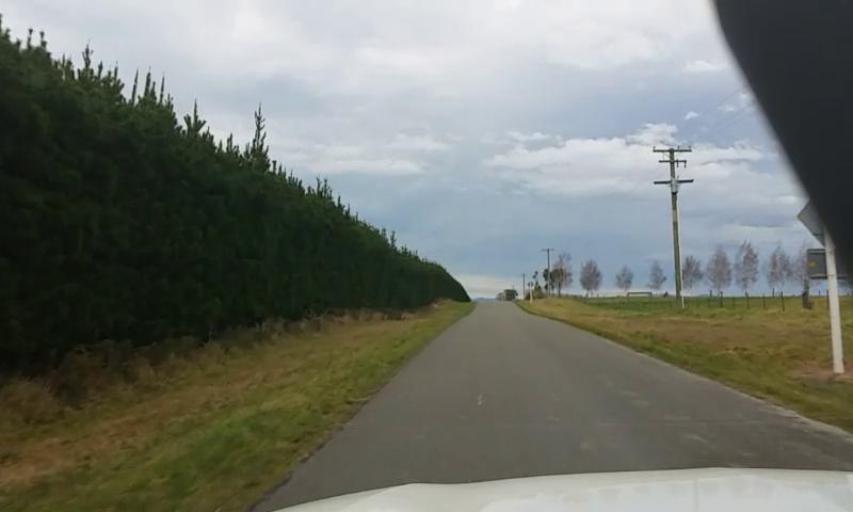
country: NZ
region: Canterbury
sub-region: Waimakariri District
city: Kaiapoi
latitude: -43.2919
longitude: 172.4710
